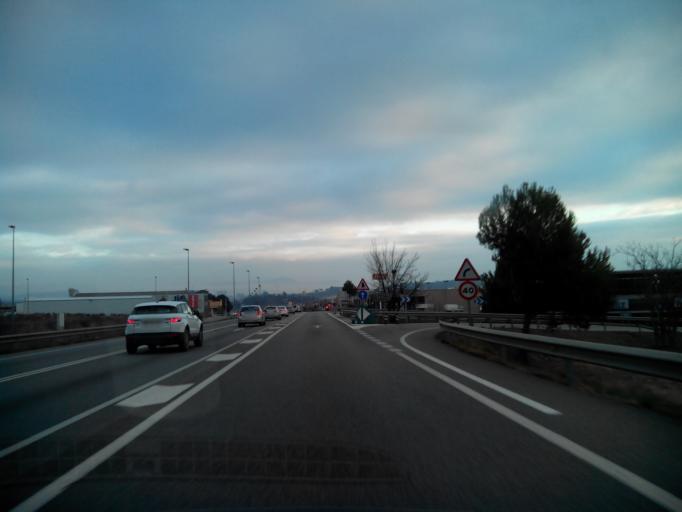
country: ES
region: Catalonia
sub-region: Provincia de Barcelona
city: Sant Fruitos de Bages
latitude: 41.7458
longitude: 1.8583
